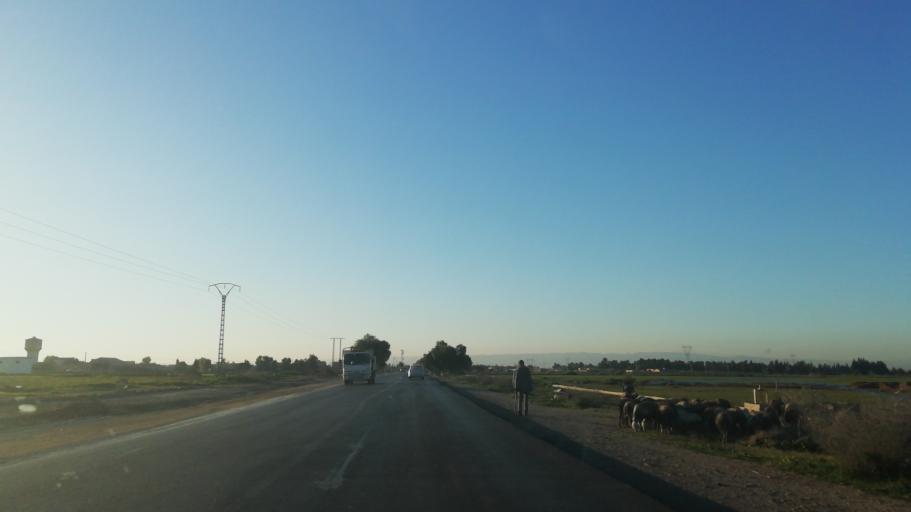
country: DZ
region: Relizane
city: Relizane
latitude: 35.7634
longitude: 0.6472
